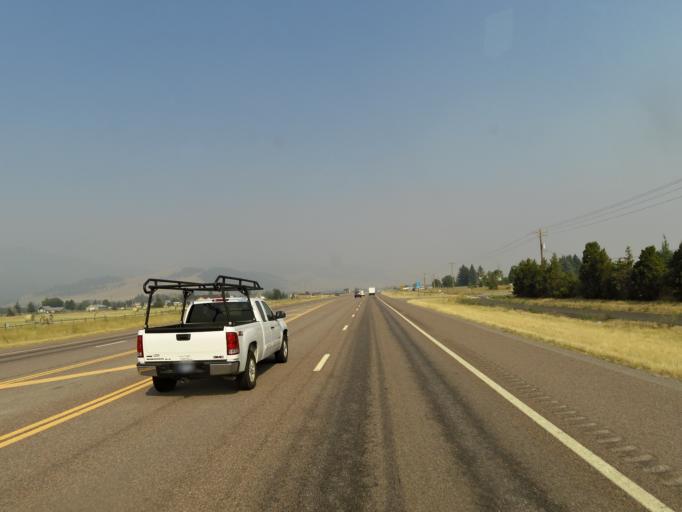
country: US
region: Montana
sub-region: Missoula County
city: Frenchtown
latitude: 47.1466
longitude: -114.0560
